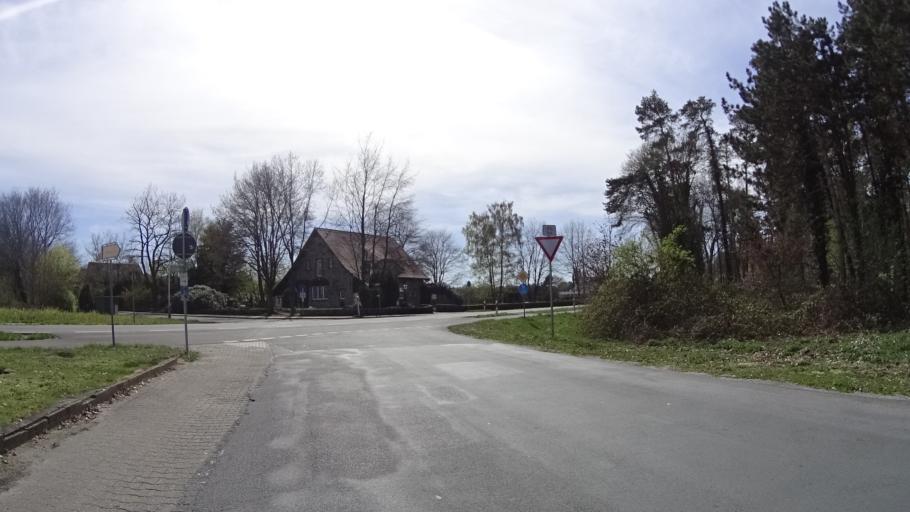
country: DE
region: Lower Saxony
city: Spelle
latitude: 52.3492
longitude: 7.4430
